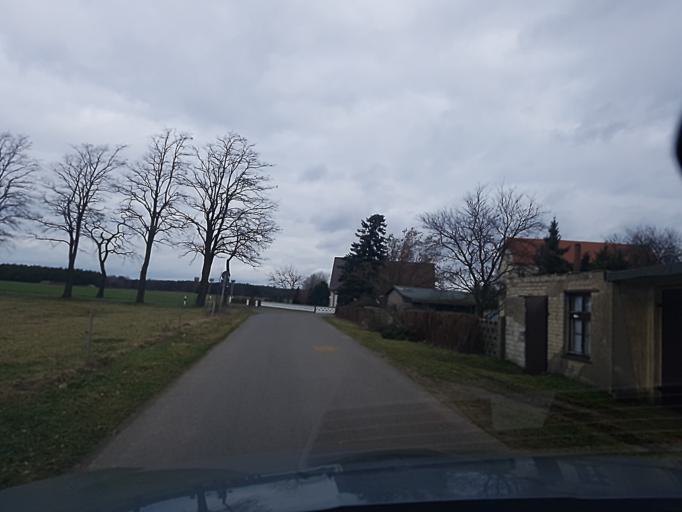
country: DE
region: Brandenburg
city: Bad Liebenwerda
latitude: 51.5538
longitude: 13.3583
